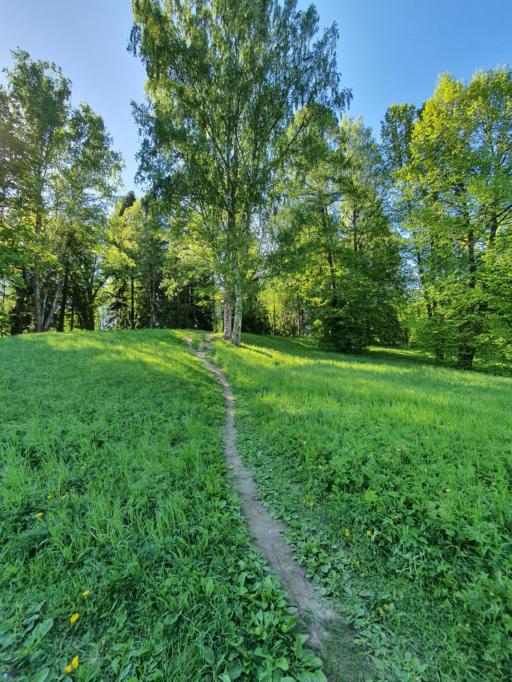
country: RU
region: St.-Petersburg
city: Tyarlevo
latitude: 59.6908
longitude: 30.4570
